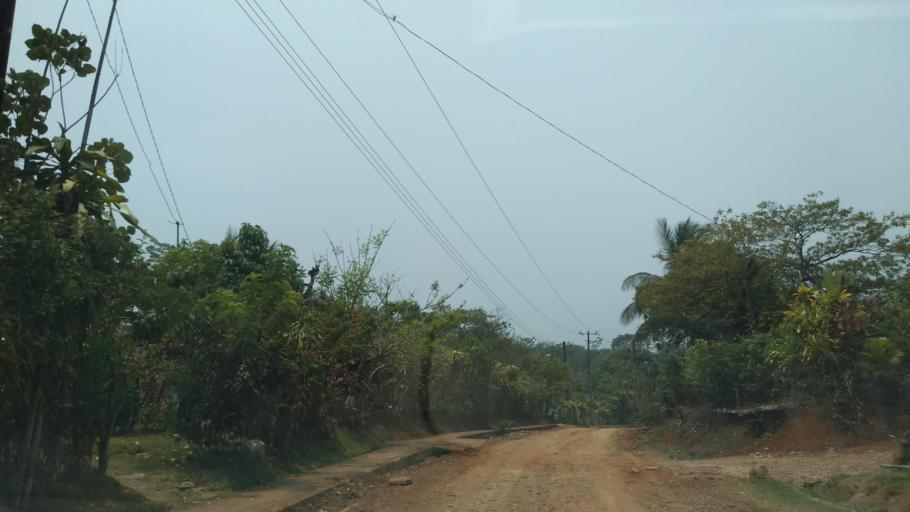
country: MX
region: Puebla
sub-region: San Sebastian Tlacotepec
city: San Martin Mazateopan
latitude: 18.4948
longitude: -96.7797
